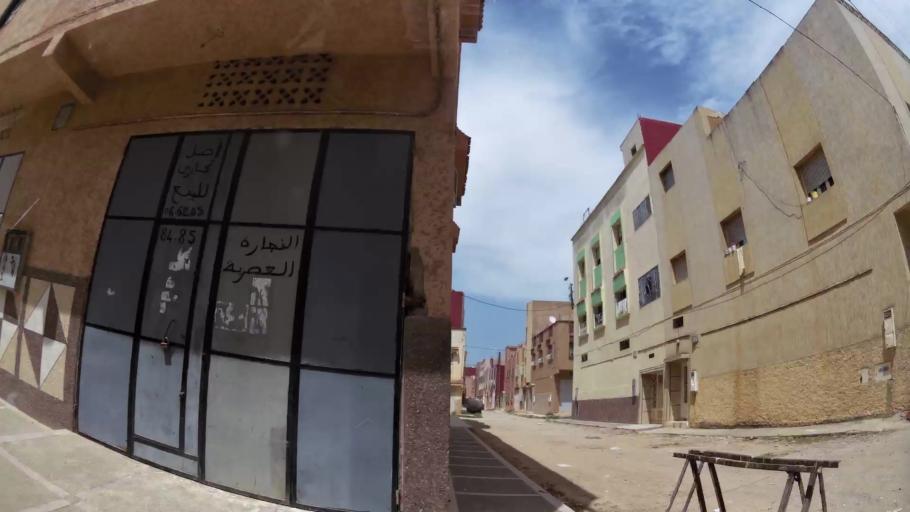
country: MA
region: Rabat-Sale-Zemmour-Zaer
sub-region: Khemisset
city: Khemisset
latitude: 33.8169
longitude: -6.0692
